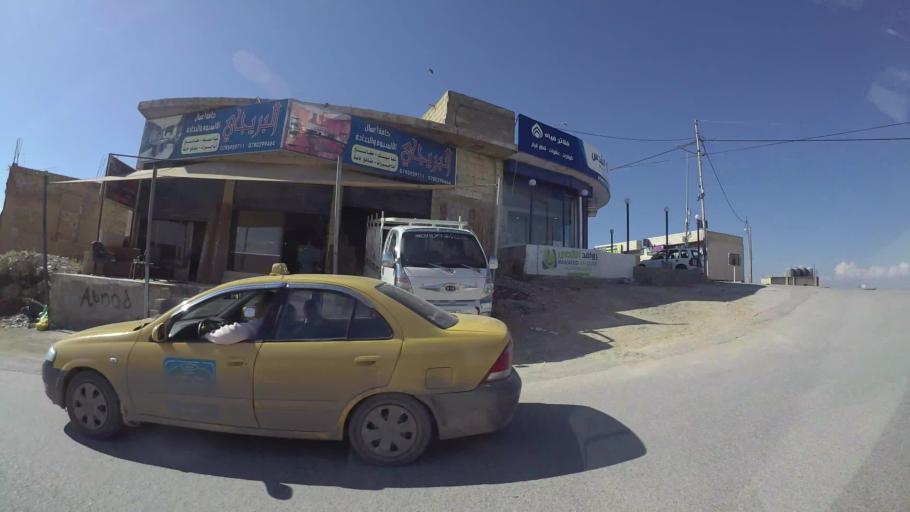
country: JO
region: Zarqa
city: Russeifa
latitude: 32.0406
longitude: 36.0532
